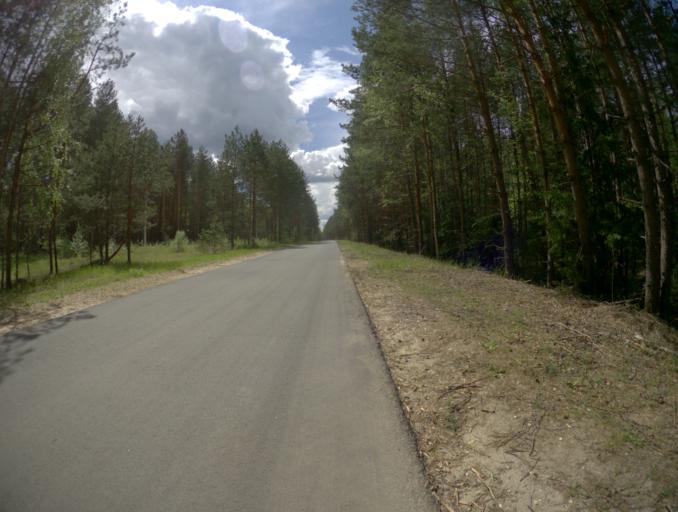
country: RU
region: Vladimir
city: Velikodvorskiy
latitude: 55.2514
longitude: 40.7691
